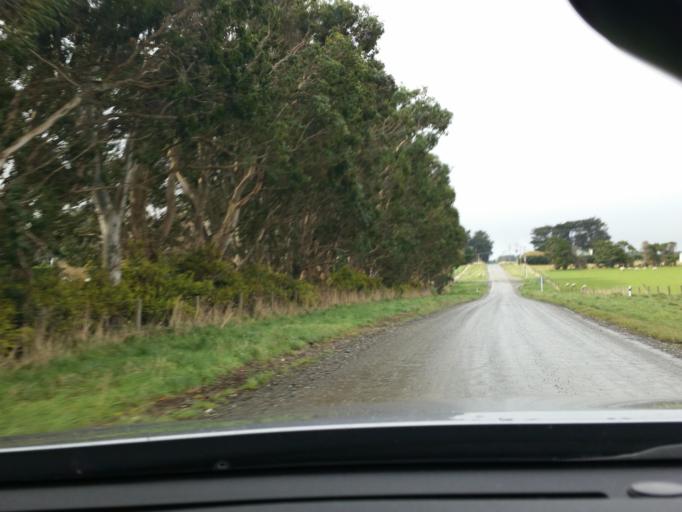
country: NZ
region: Southland
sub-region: Invercargill City
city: Invercargill
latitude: -46.3558
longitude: 168.4324
